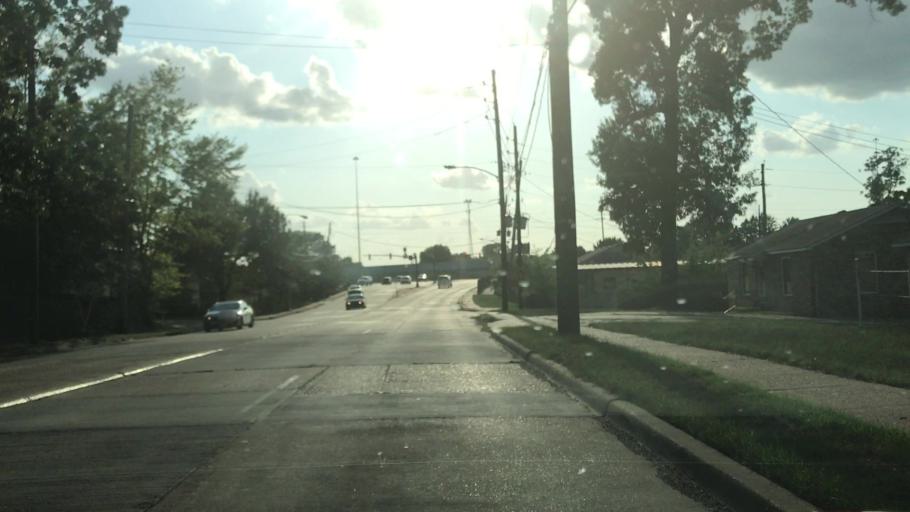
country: US
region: Louisiana
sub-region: Bossier Parish
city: Bossier City
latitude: 32.4548
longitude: -93.7528
